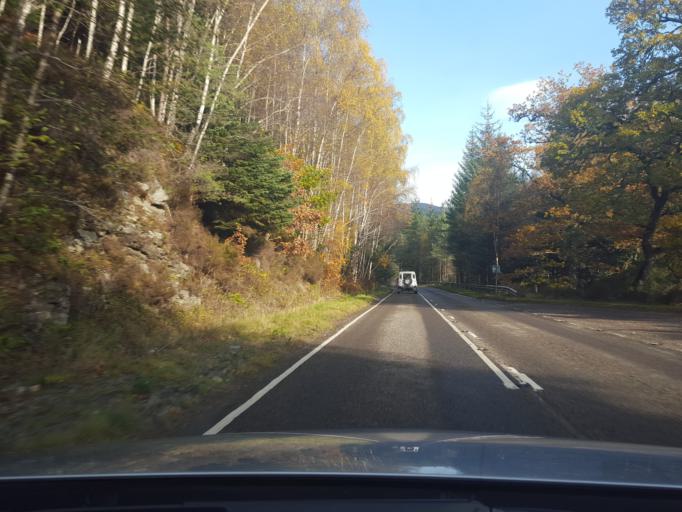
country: GB
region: Scotland
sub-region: Highland
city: Beauly
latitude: 57.2058
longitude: -4.7000
